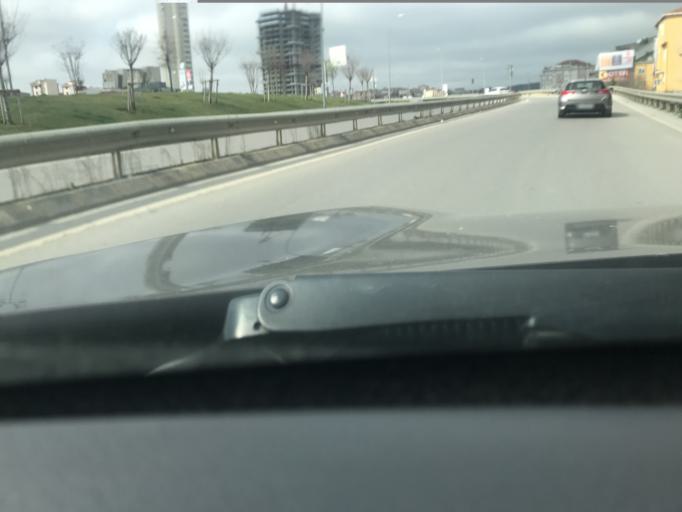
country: TR
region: Istanbul
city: Umraniye
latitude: 41.0303
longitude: 29.1724
